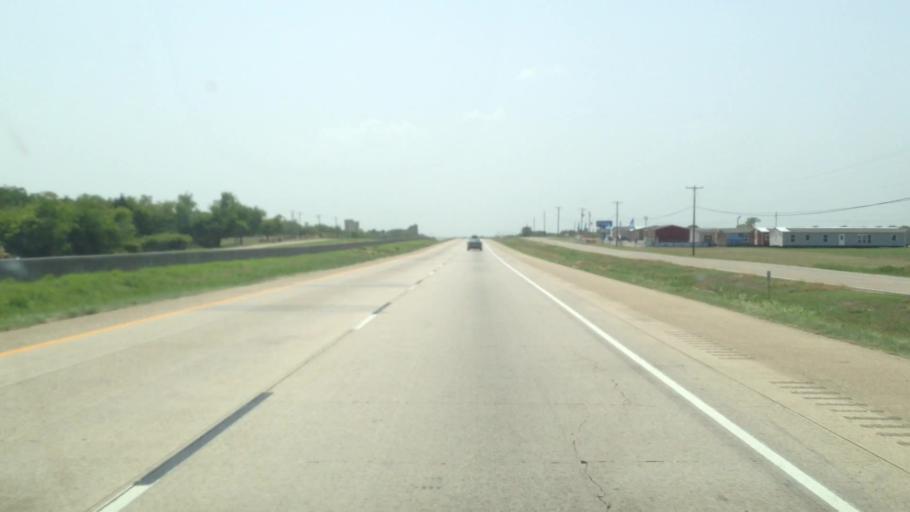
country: US
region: Texas
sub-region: Hopkins County
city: Sulphur Springs
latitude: 33.1210
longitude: -95.6519
